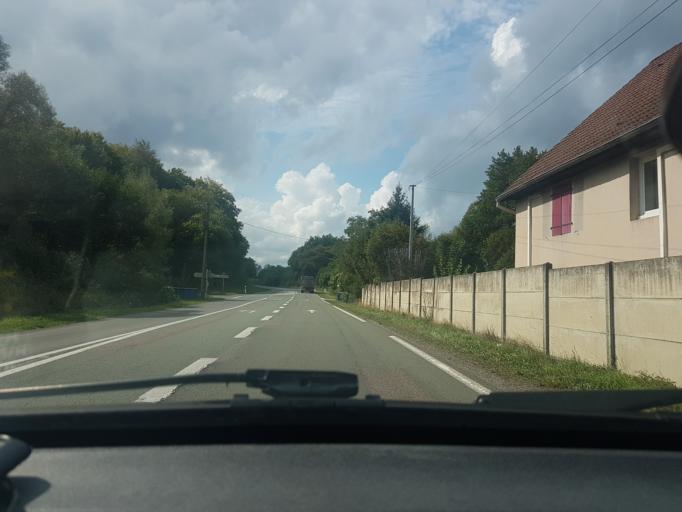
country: FR
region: Franche-Comte
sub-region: Departement de la Haute-Saone
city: Hericourt
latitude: 47.5930
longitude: 6.7102
